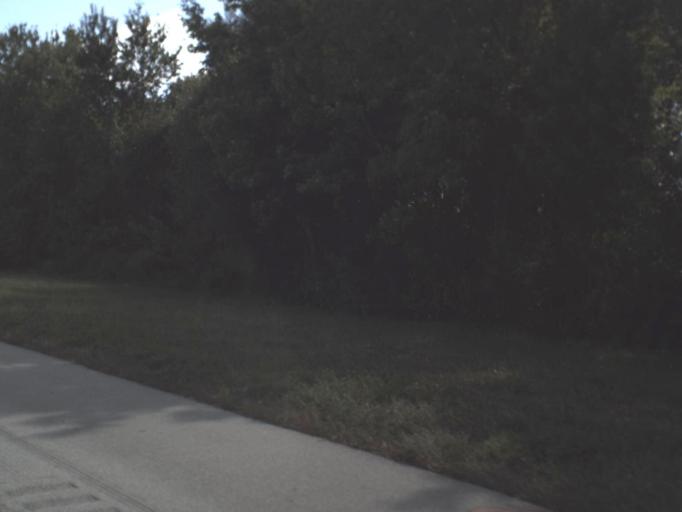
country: US
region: Florida
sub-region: Osceola County
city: Saint Cloud
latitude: 28.0598
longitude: -81.2322
